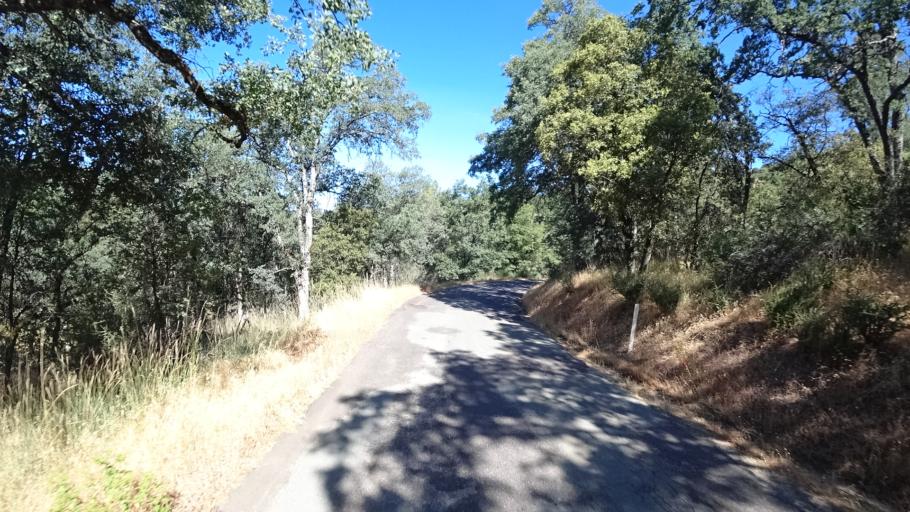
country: US
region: California
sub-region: Amador County
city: Pioneer
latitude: 38.3958
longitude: -120.4752
